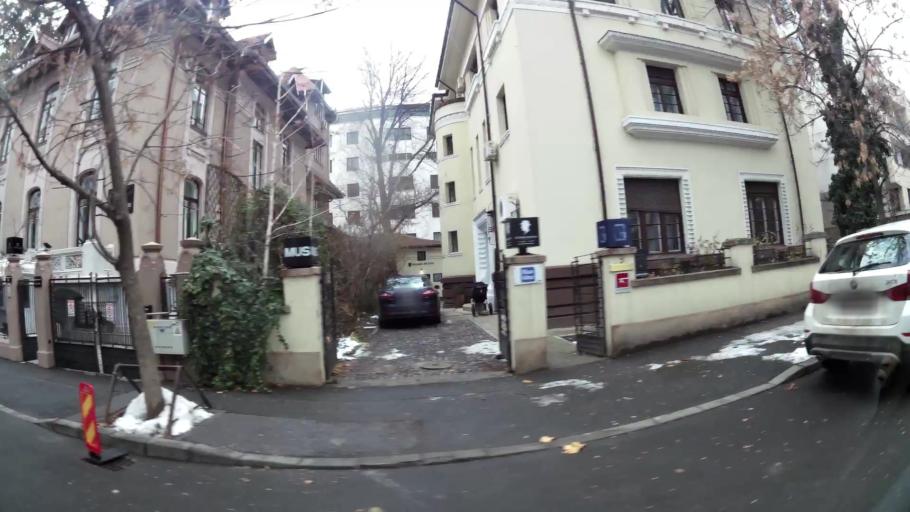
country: RO
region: Bucuresti
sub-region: Municipiul Bucuresti
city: Bucuresti
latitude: 44.4557
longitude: 26.0880
